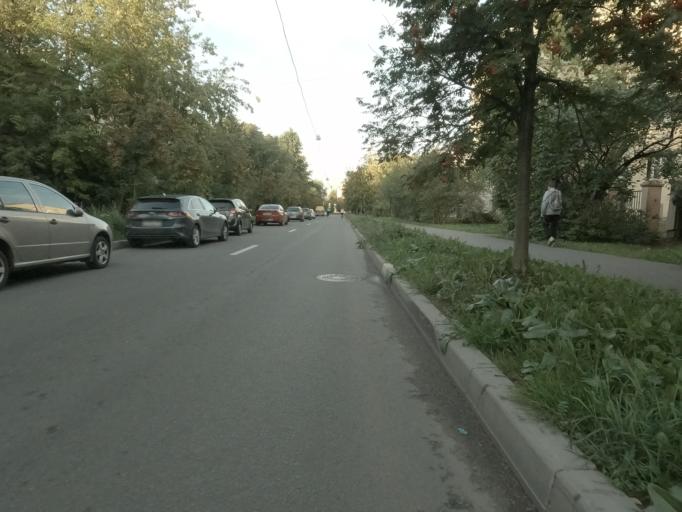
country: RU
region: St.-Petersburg
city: Admiralteisky
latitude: 59.8968
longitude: 30.2687
